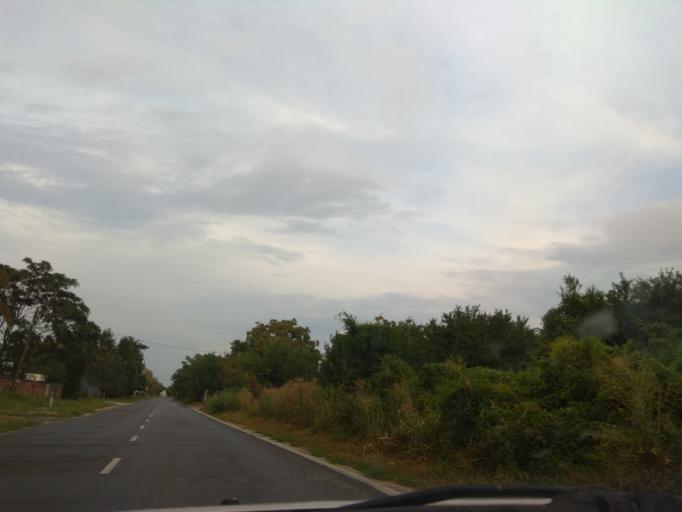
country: HU
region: Borsod-Abauj-Zemplen
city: Miskolc
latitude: 48.1010
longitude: 20.8249
